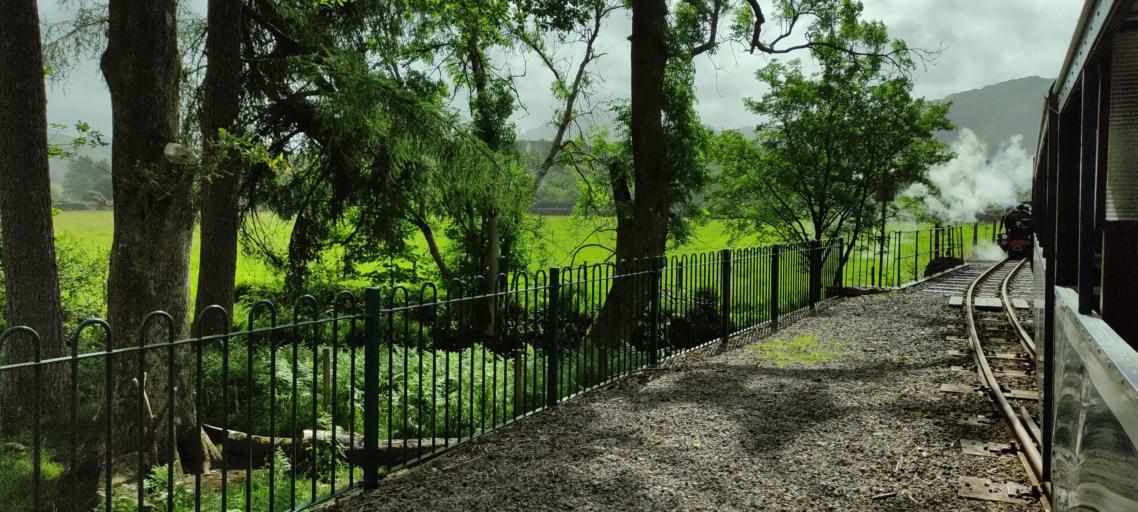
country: GB
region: England
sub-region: Cumbria
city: Millom
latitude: 54.3958
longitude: -3.2754
